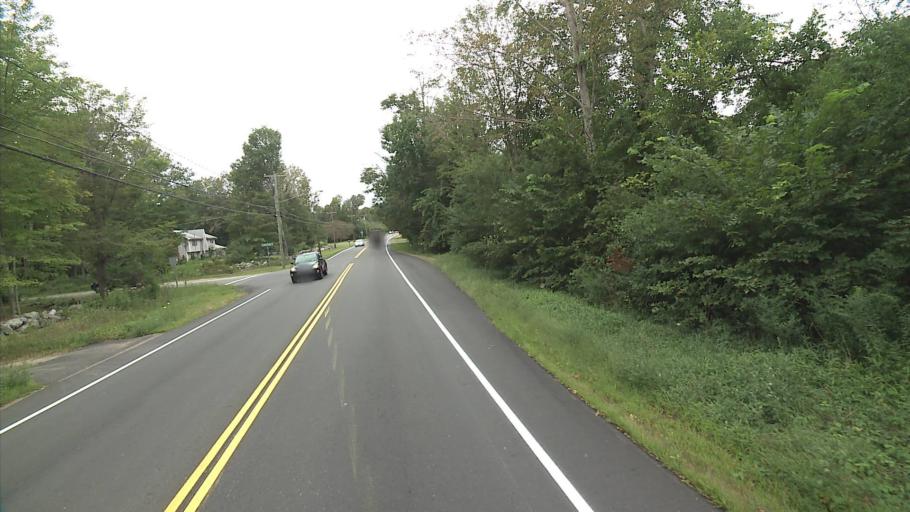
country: US
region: Connecticut
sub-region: Tolland County
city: Hebron
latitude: 41.6447
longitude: -72.3574
